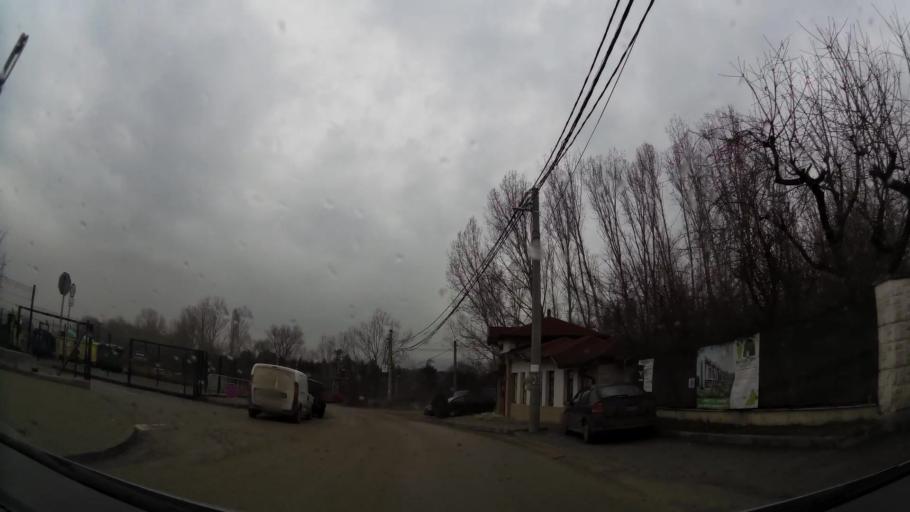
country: BG
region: Sofia-Capital
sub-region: Stolichna Obshtina
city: Sofia
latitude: 42.6207
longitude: 23.3789
